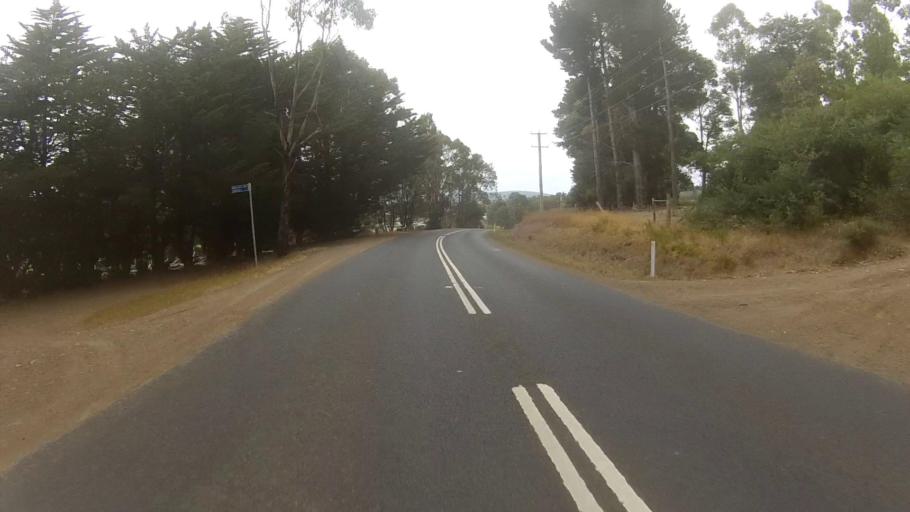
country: AU
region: Tasmania
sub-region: Kingborough
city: Margate
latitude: -43.0182
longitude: 147.2531
